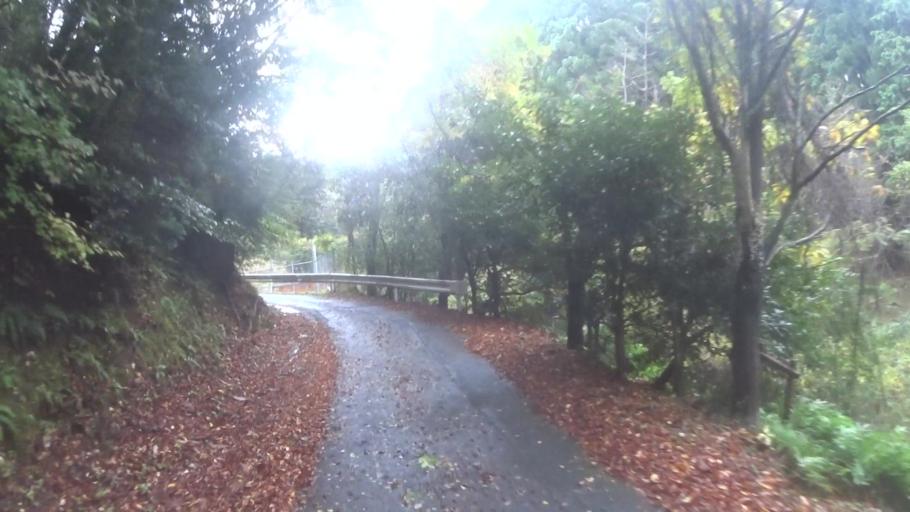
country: JP
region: Kyoto
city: Miyazu
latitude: 35.4889
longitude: 135.1251
